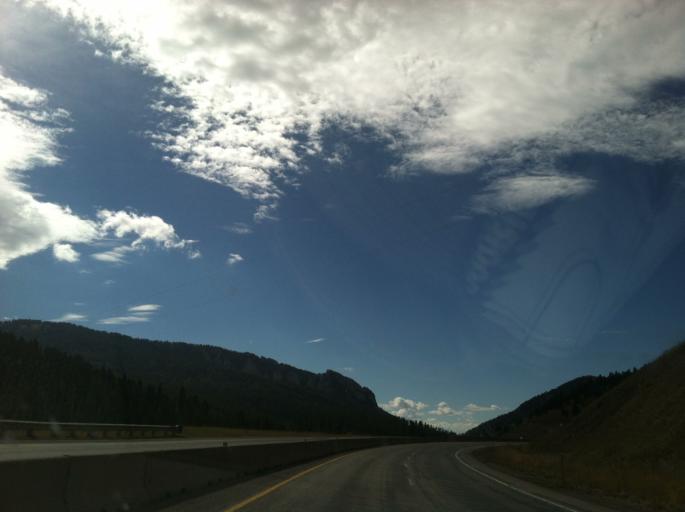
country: US
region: Montana
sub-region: Gallatin County
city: Bozeman
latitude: 45.6484
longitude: -110.8642
